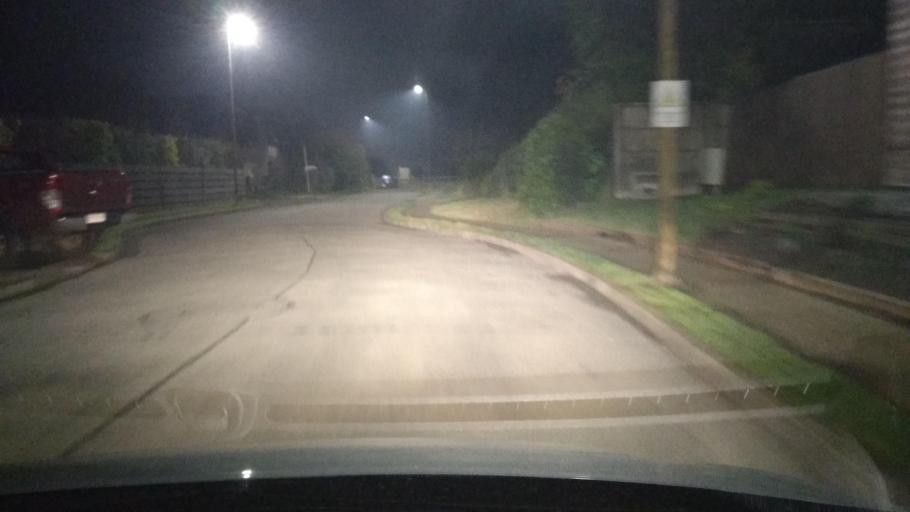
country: CL
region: Los Rios
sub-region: Provincia de Valdivia
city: Valdivia
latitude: -39.8189
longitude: -73.2550
